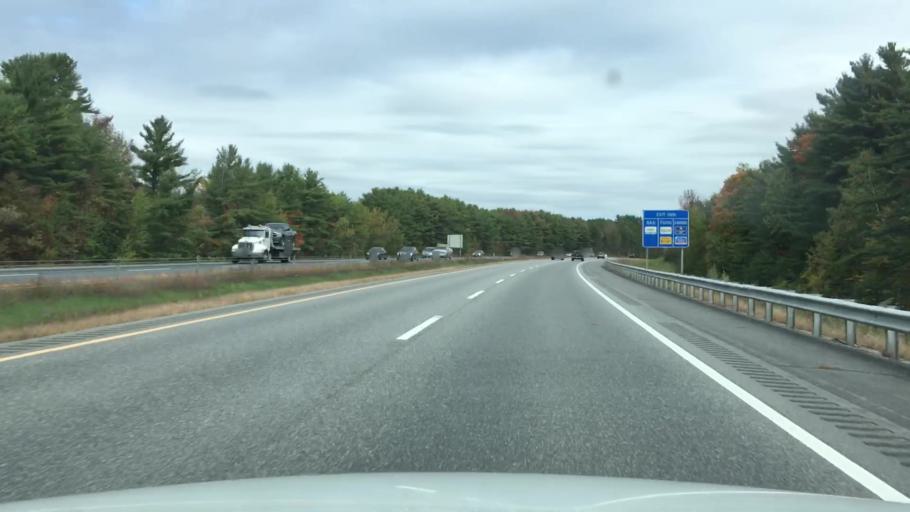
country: US
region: Maine
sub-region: Kennebec County
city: Augusta
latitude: 44.3312
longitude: -69.8137
